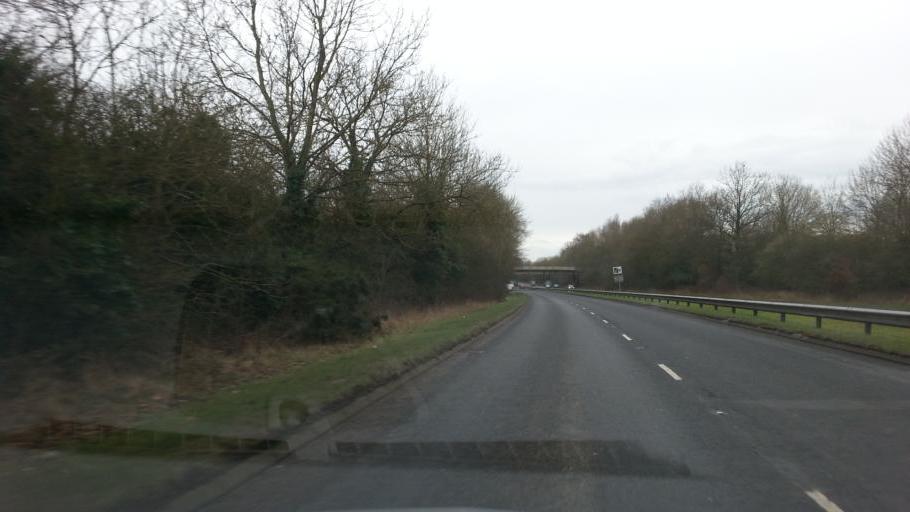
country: GB
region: England
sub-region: Solihull
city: Tidbury Green
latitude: 52.3957
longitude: -1.8955
